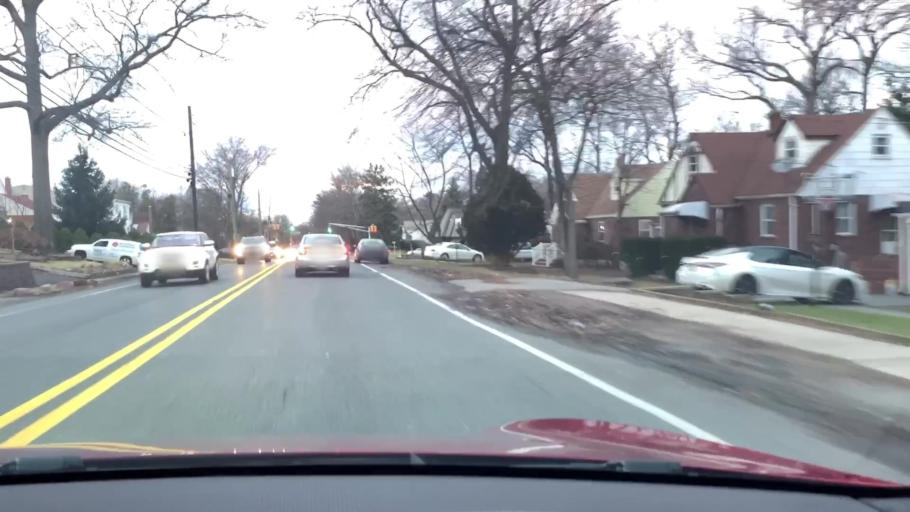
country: US
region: New Jersey
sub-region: Bergen County
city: Demarest
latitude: 40.9464
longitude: -73.9763
